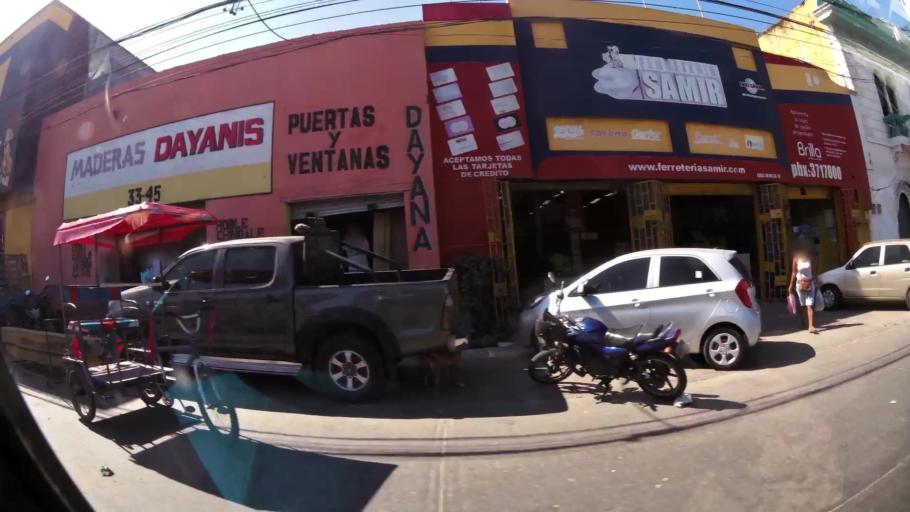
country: CO
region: Atlantico
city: Barranquilla
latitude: 10.9723
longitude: -74.7794
